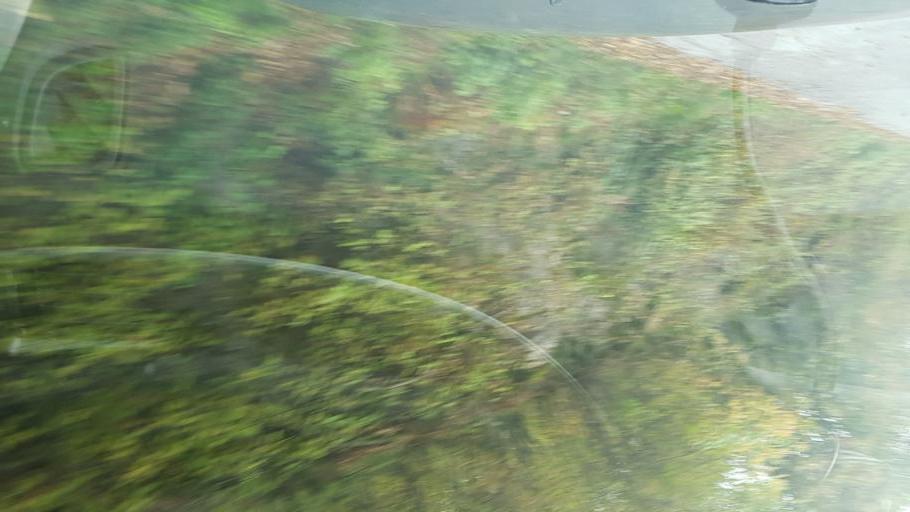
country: HR
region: Istarska
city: Buzet
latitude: 45.4606
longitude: 14.0331
